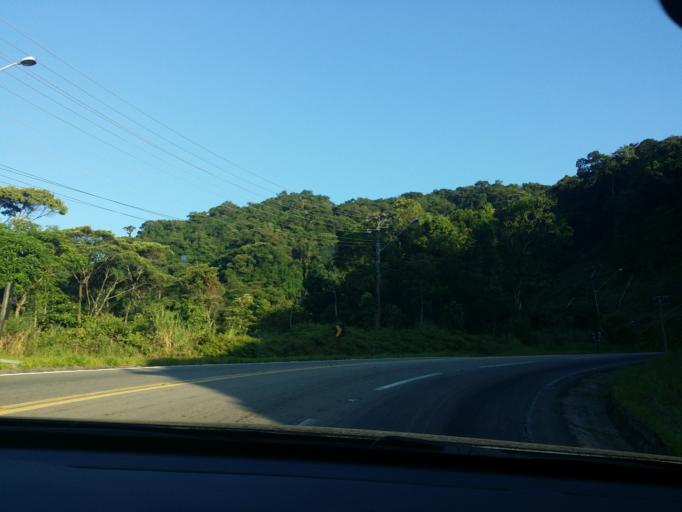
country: BR
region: Sao Paulo
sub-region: Sao Sebastiao
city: Sao Sebastiao
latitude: -23.7810
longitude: -45.6088
